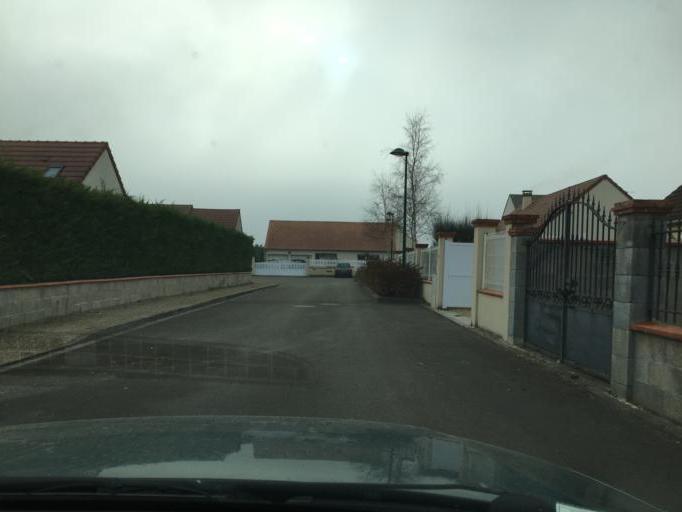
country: FR
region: Centre
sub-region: Departement du Loiret
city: Saran
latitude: 47.9887
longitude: 1.8884
